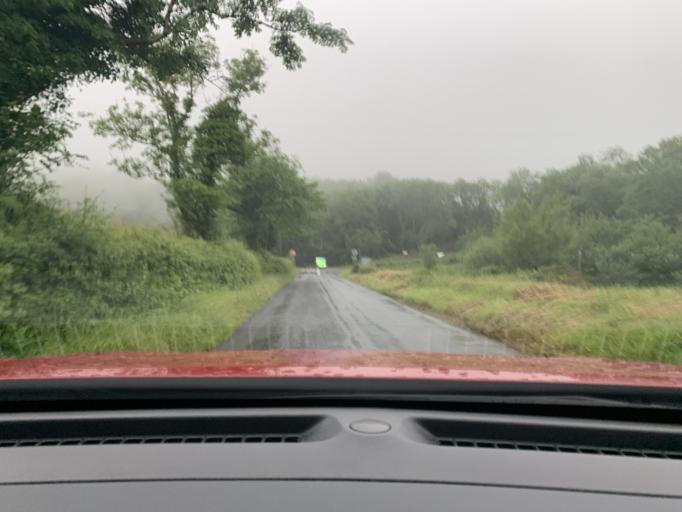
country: IE
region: Connaught
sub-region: Sligo
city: Sligo
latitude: 54.3233
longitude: -8.4247
